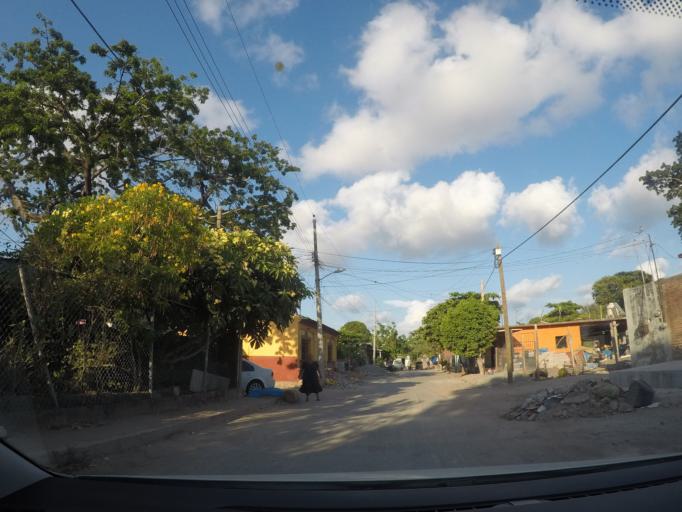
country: MX
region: Oaxaca
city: Juchitan de Zaragoza
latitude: 16.4359
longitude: -95.0275
